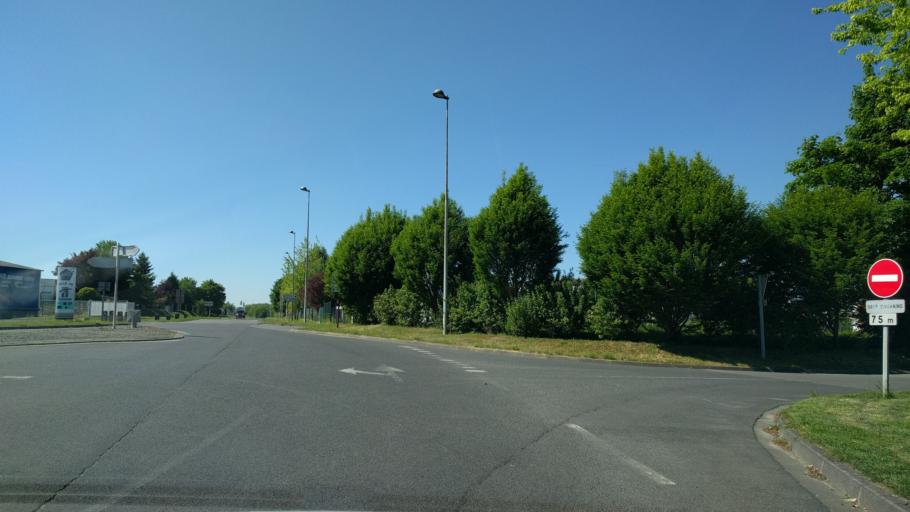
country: FR
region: Picardie
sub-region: Departement de la Somme
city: Peronne
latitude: 49.9133
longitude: 2.9304
